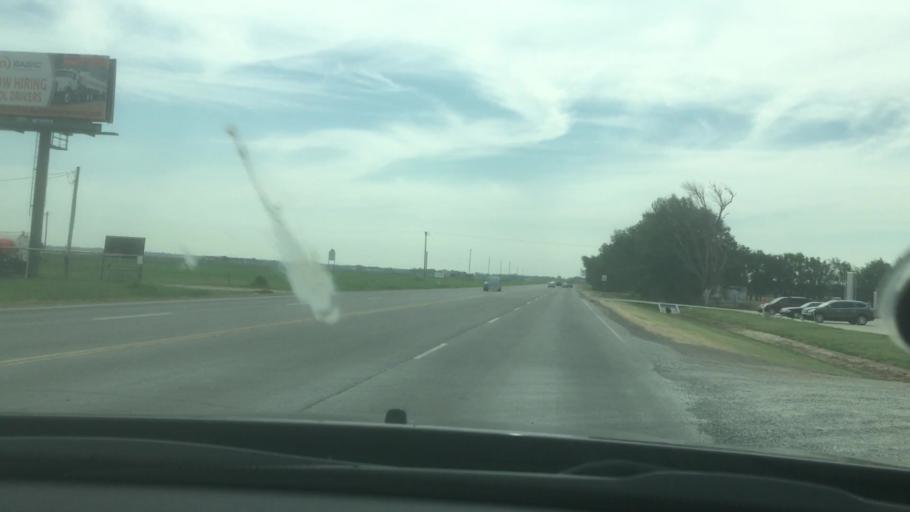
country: US
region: Oklahoma
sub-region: Garvin County
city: Lindsay
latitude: 34.8363
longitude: -97.5951
